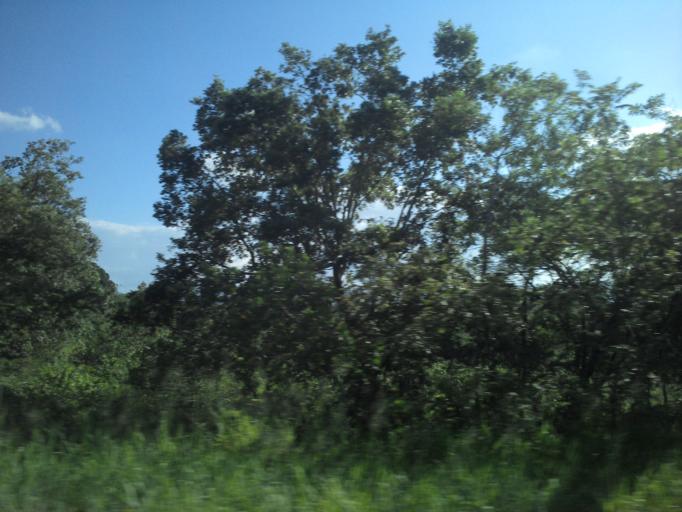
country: MX
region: Chiapas
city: Palenque
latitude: 17.5526
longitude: -91.9883
